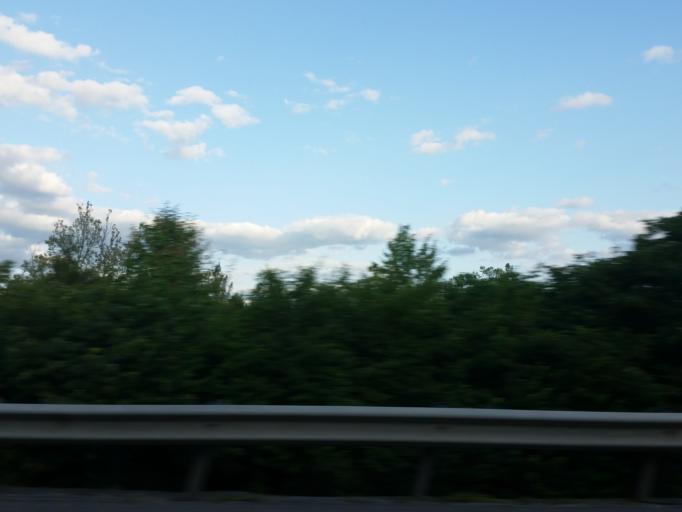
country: US
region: Virginia
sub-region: Washington County
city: Abingdon
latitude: 36.6594
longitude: -82.0669
